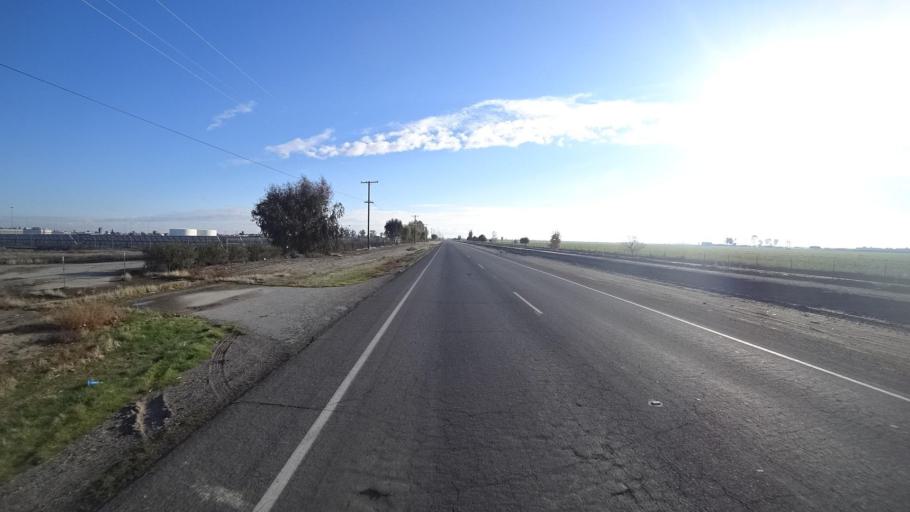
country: US
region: California
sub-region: Kern County
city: Delano
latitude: 35.7759
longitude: -119.3115
